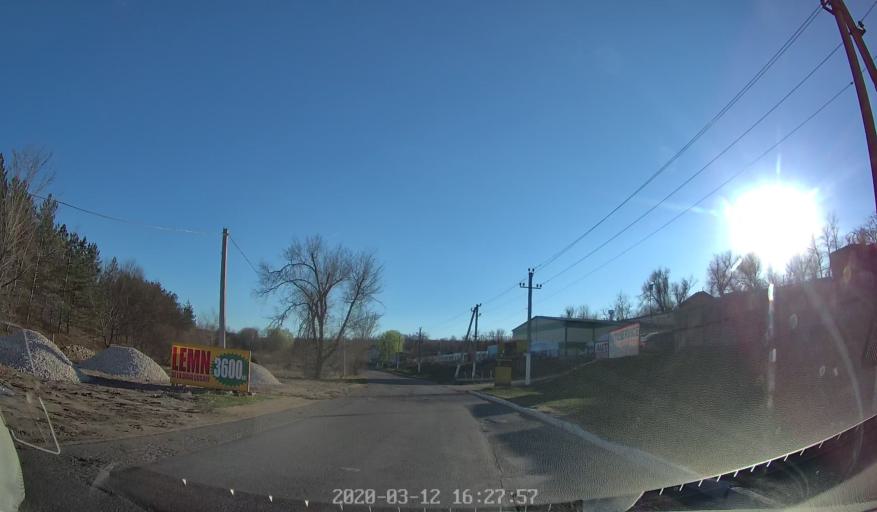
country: MD
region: Anenii Noi
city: Anenii Noi
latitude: 46.8720
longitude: 29.2267
